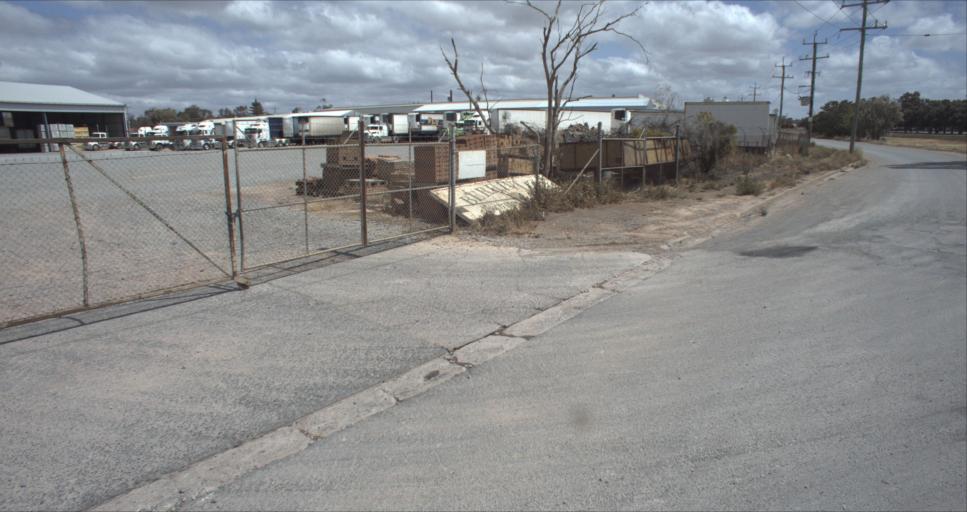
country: AU
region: New South Wales
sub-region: Leeton
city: Leeton
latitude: -34.5522
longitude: 146.3909
